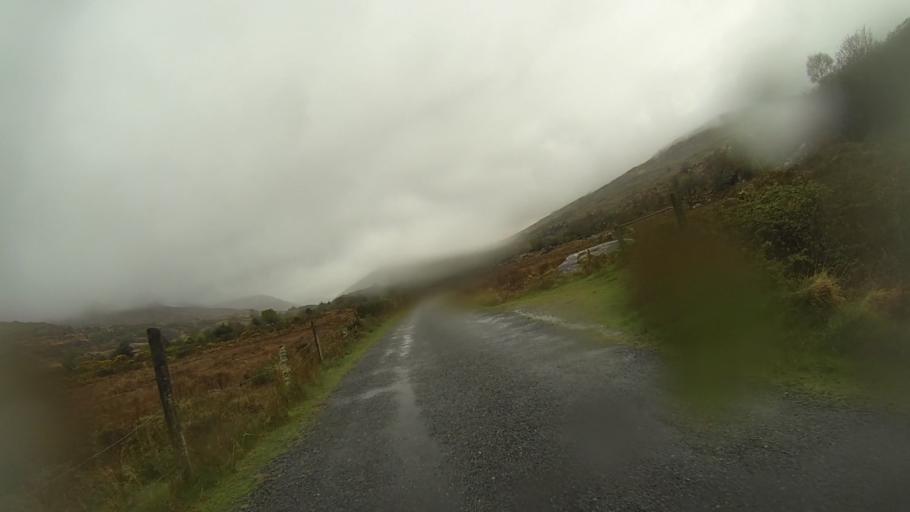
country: IE
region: Munster
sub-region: Ciarrai
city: Kenmare
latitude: 51.9488
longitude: -9.6624
